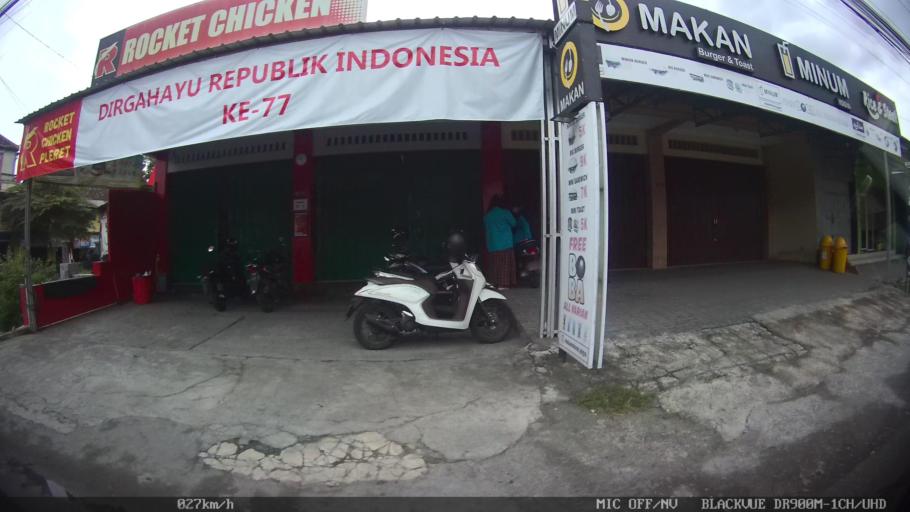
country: ID
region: Daerah Istimewa Yogyakarta
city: Sewon
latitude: -7.8429
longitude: 110.4111
